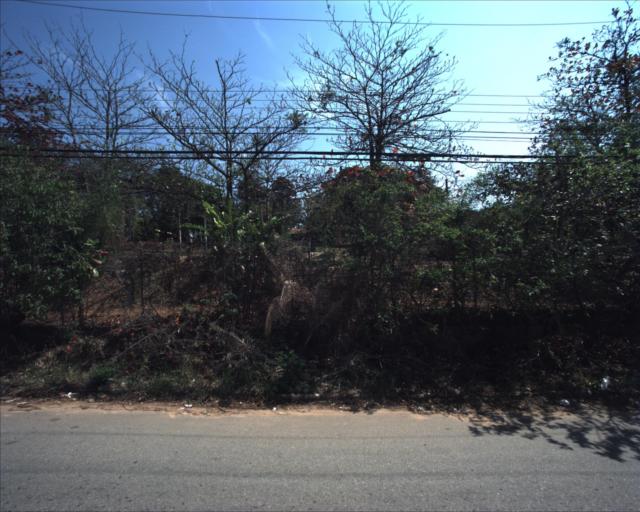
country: BR
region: Sao Paulo
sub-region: Sorocaba
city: Sorocaba
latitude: -23.4524
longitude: -47.4962
